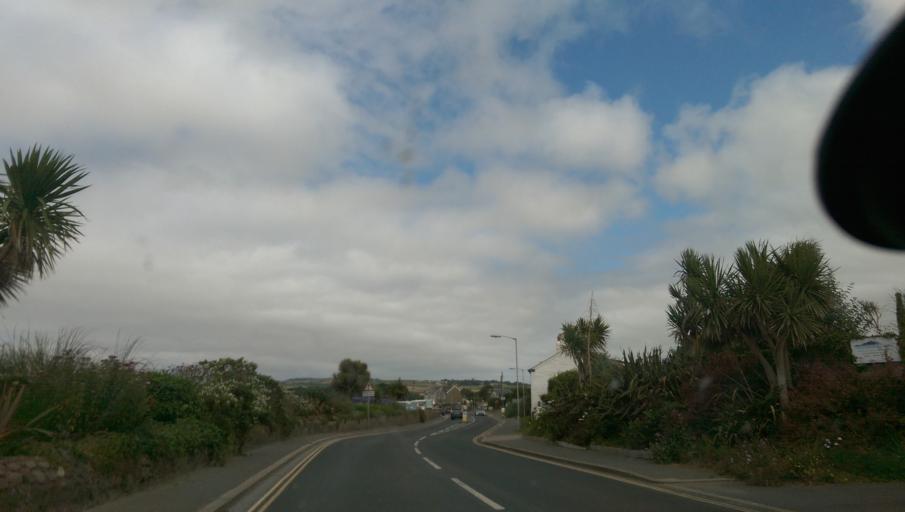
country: GB
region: England
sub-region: Cornwall
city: Marazion
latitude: 50.1254
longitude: -5.4772
